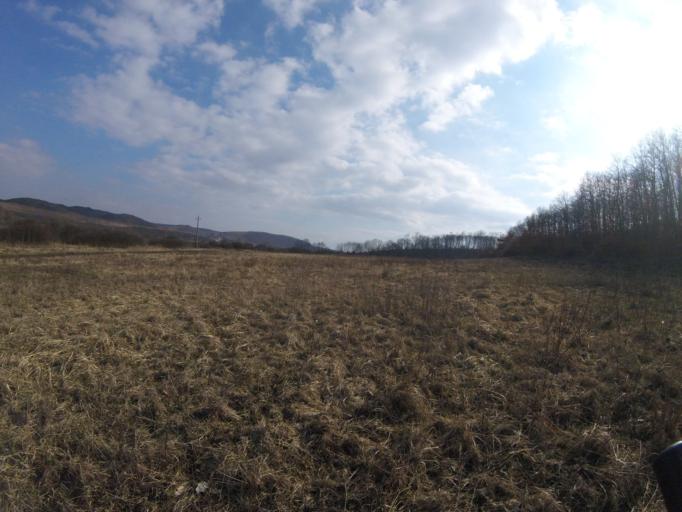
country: HU
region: Heves
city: Egerszalok
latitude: 47.8463
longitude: 20.3250
